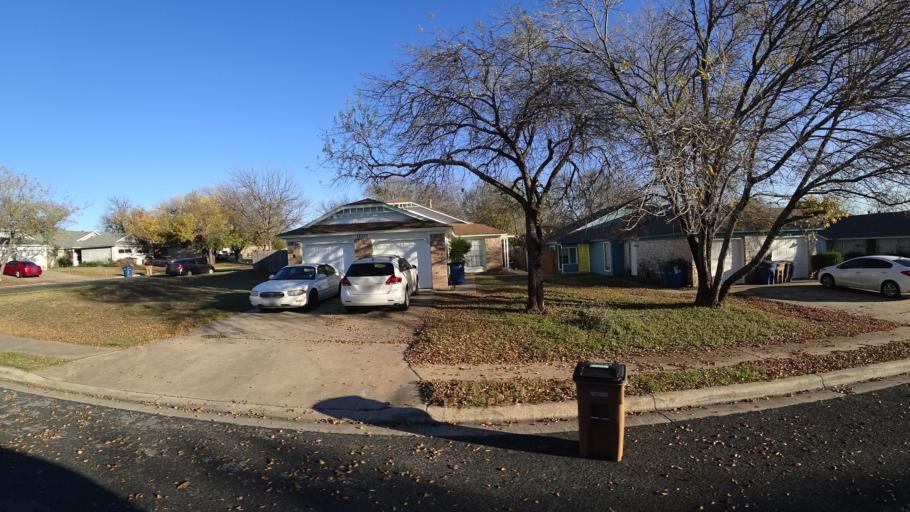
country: US
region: Texas
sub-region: Travis County
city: Wells Branch
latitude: 30.4119
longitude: -97.6989
